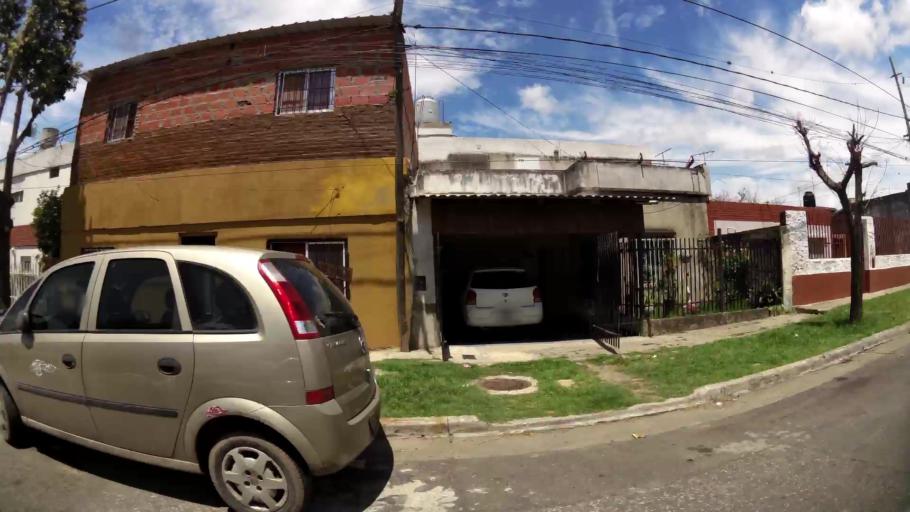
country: AR
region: Santa Fe
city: Gobernador Galvez
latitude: -32.9963
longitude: -60.6213
